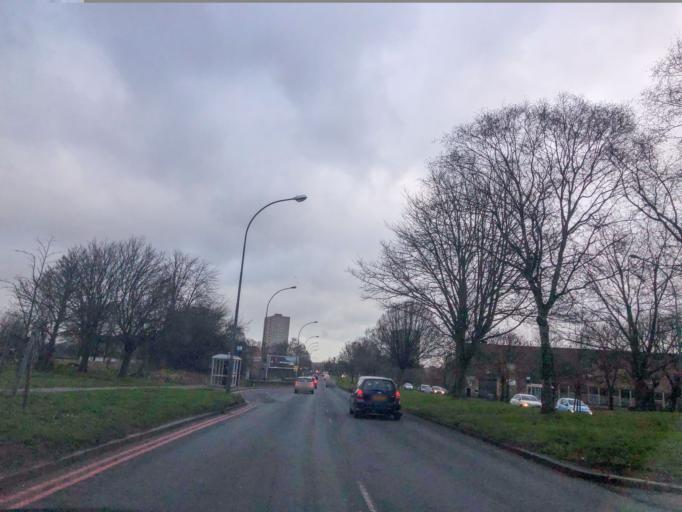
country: GB
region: England
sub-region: City and Borough of Birmingham
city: Hockley
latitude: 52.4798
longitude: -1.9262
